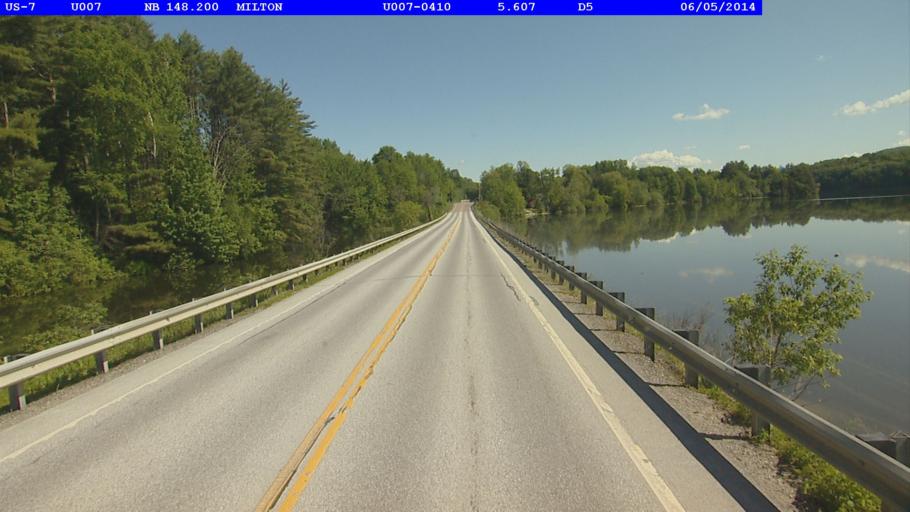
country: US
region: Vermont
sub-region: Chittenden County
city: Milton
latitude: 44.6476
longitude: -73.1161
